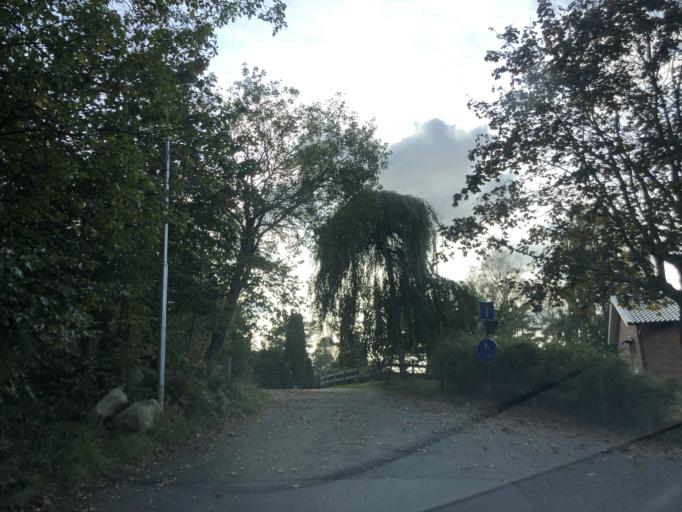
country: SE
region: Vaestra Goetaland
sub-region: Goteborg
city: Billdal
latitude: 57.6317
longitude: 11.9433
